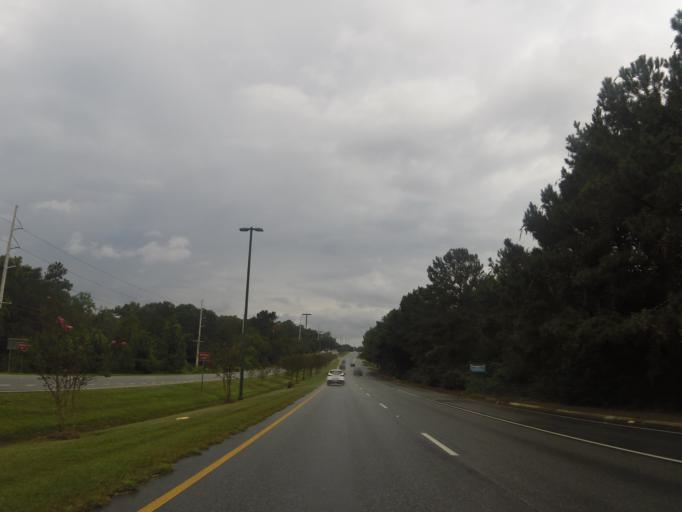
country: US
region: Alabama
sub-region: Baldwin County
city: Fairhope
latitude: 30.5517
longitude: -87.8915
